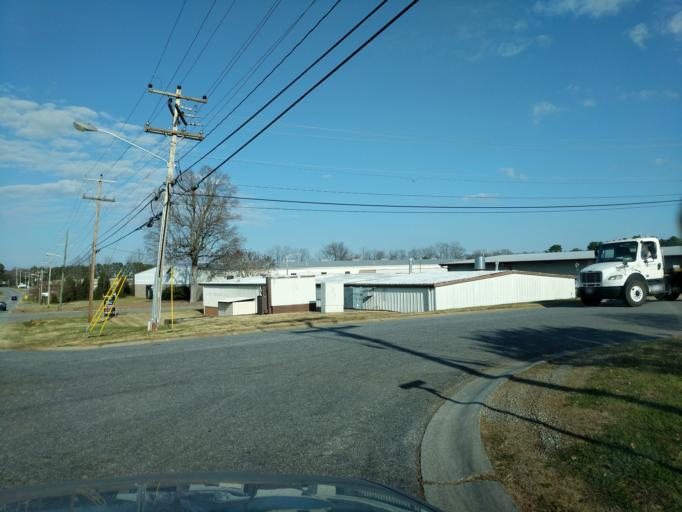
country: US
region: North Carolina
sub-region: Iredell County
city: Statesville
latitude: 35.7917
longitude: -80.9229
